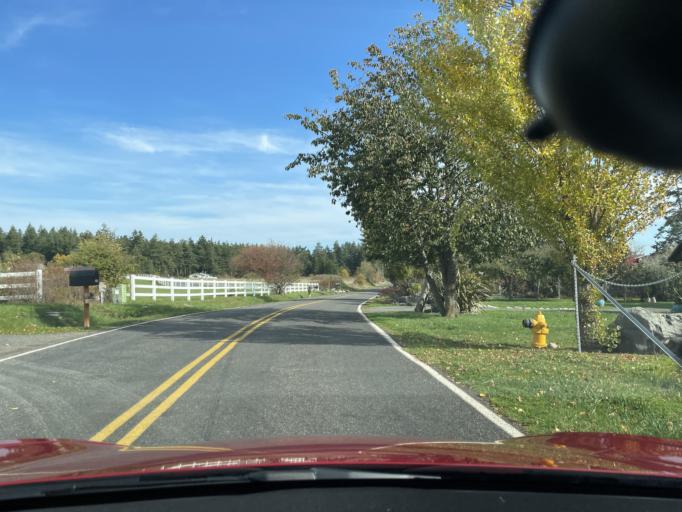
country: US
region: Washington
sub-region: San Juan County
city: Friday Harbor
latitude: 48.5195
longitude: -122.9796
